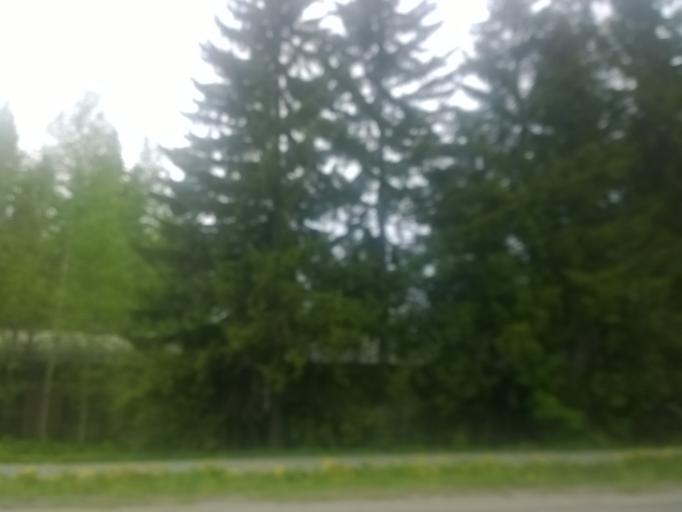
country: FI
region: Pirkanmaa
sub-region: Tampere
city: Lempaeaelae
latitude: 61.3353
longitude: 23.7505
